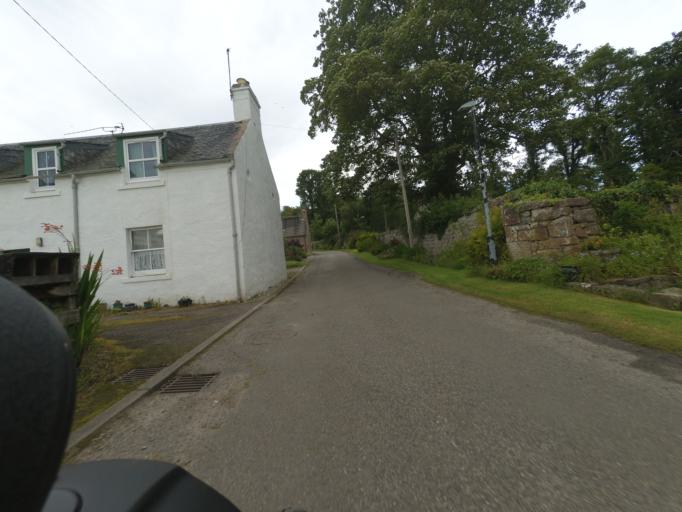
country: GB
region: Scotland
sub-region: Highland
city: Conon Bridge
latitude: 57.5123
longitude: -4.3675
